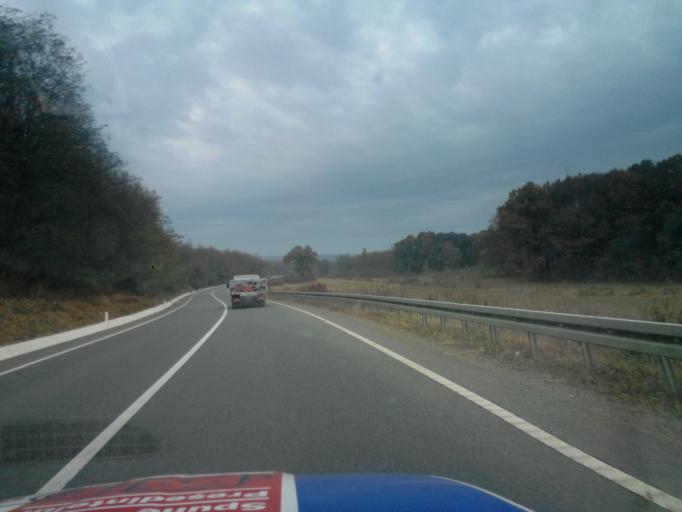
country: RO
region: Vaslui
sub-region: Comuna Tatarani
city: Tatarani
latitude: 46.6628
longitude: 27.9866
